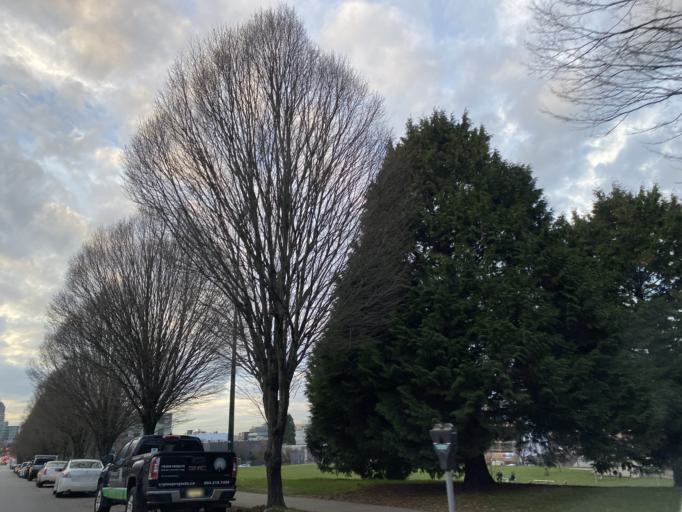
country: CA
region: British Columbia
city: Vancouver
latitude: 49.2638
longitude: -123.1070
